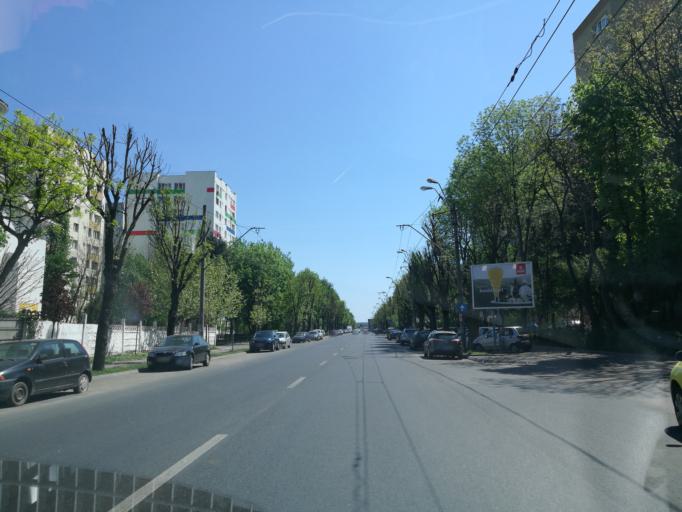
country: RO
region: Ilfov
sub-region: Comuna Popesti-Leordeni
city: Popesti-Leordeni
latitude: 44.3835
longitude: 26.1236
